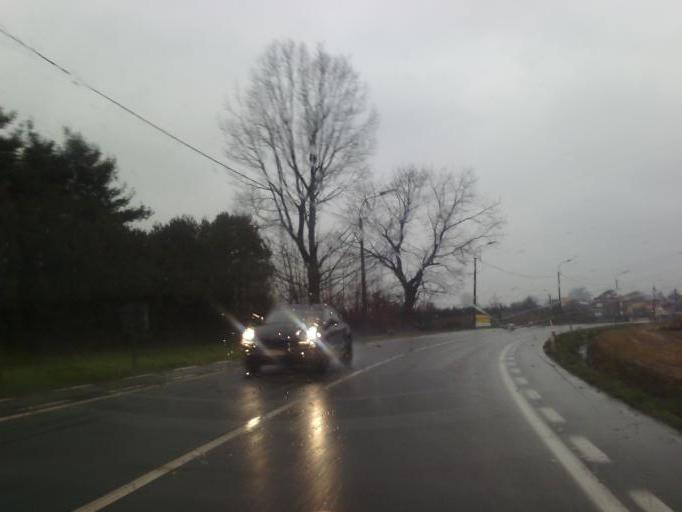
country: BE
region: Flanders
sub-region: Provincie Oost-Vlaanderen
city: Wichelen
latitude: 51.0033
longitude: 3.9455
